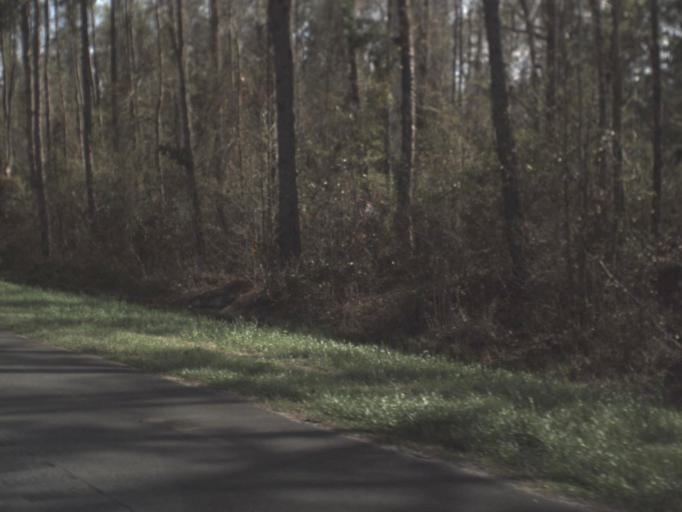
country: US
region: Florida
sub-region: Leon County
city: Tallahassee
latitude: 30.4954
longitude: -84.1742
